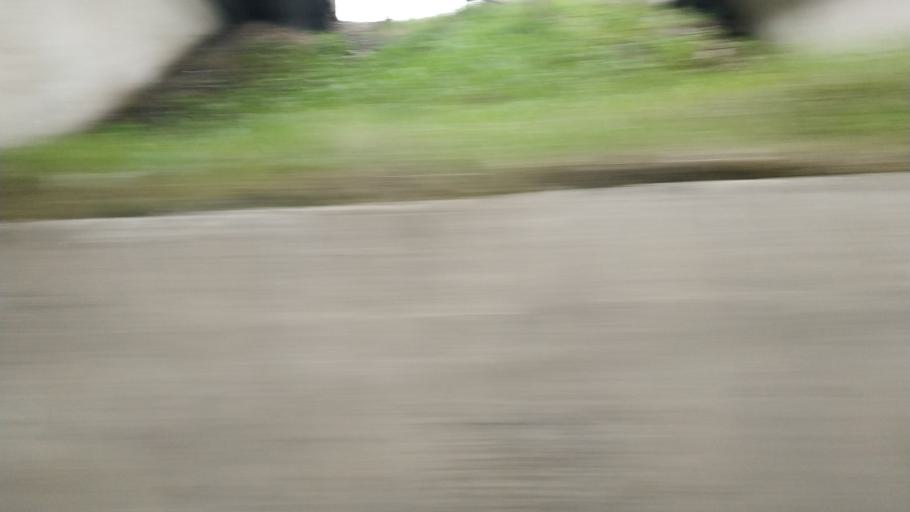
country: RU
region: Moskovskaya
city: Pavlovskiy Posad
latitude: 55.7750
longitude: 38.6863
